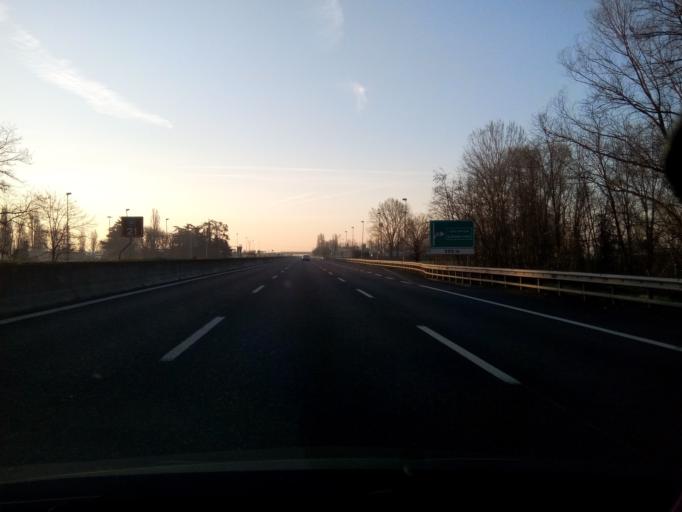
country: IT
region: Lombardy
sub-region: Citta metropolitana di Milano
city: San Zenone al Lambro
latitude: 45.3243
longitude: 9.3714
